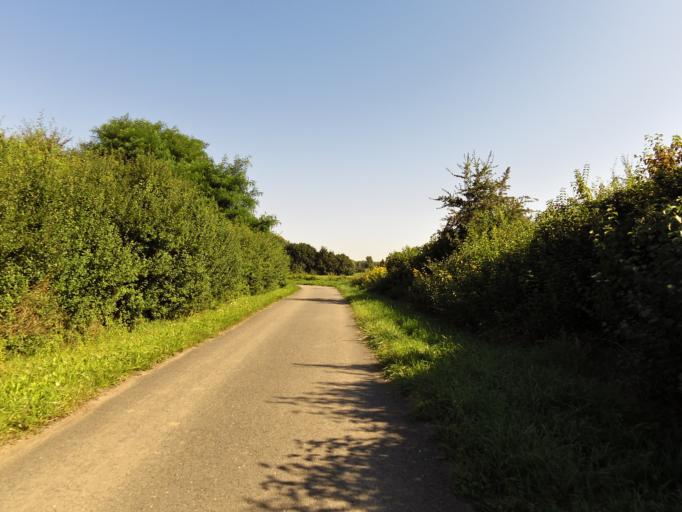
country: DE
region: Hesse
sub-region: Regierungsbezirk Darmstadt
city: Stockstadt am Rhein
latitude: 49.8023
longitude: 8.4543
